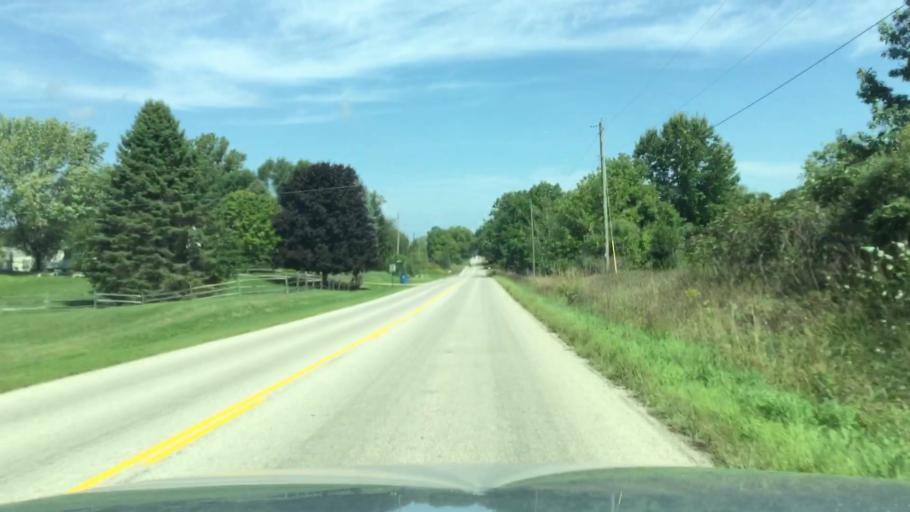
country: US
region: Michigan
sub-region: Lenawee County
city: Manitou Beach-Devils Lake
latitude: 42.0355
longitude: -84.2763
